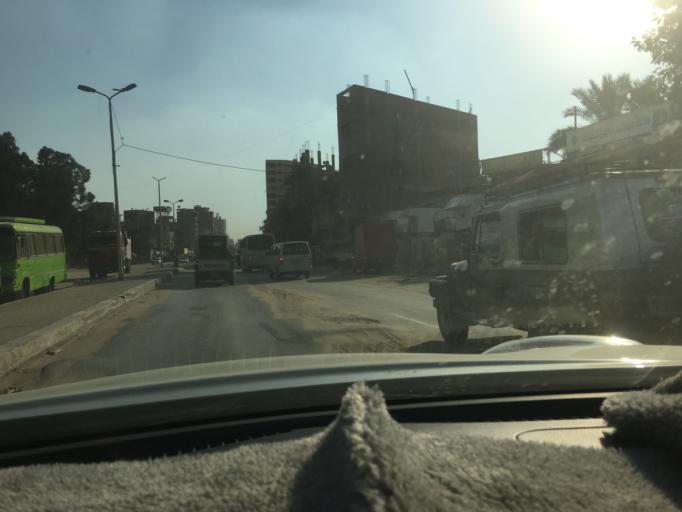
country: EG
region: Muhafazat al Qalyubiyah
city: Al Khankah
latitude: 30.1551
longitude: 31.3770
